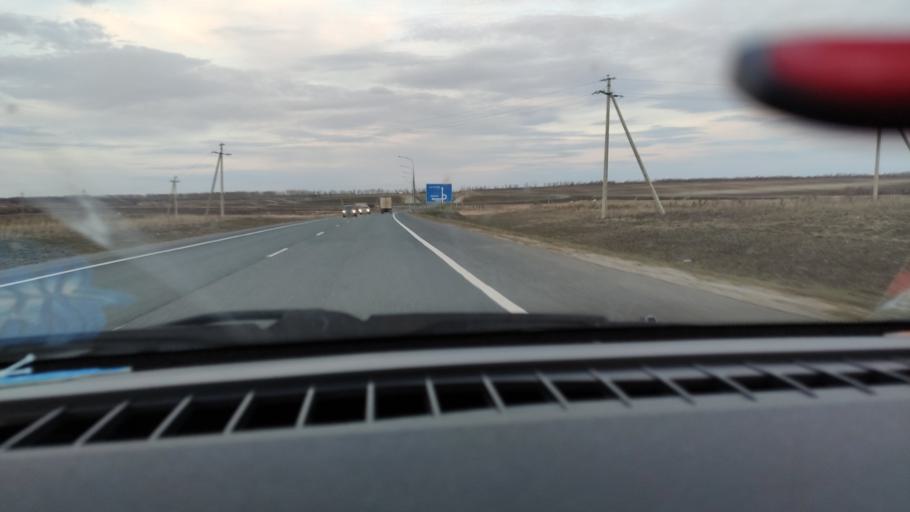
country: RU
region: Saratov
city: Yelshanka
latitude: 51.8302
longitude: 46.4172
